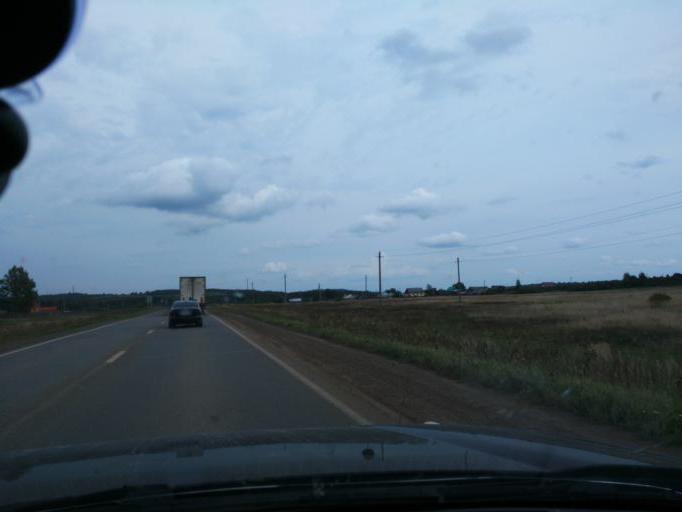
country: RU
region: Perm
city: Kuyeda
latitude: 56.4508
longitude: 55.6074
